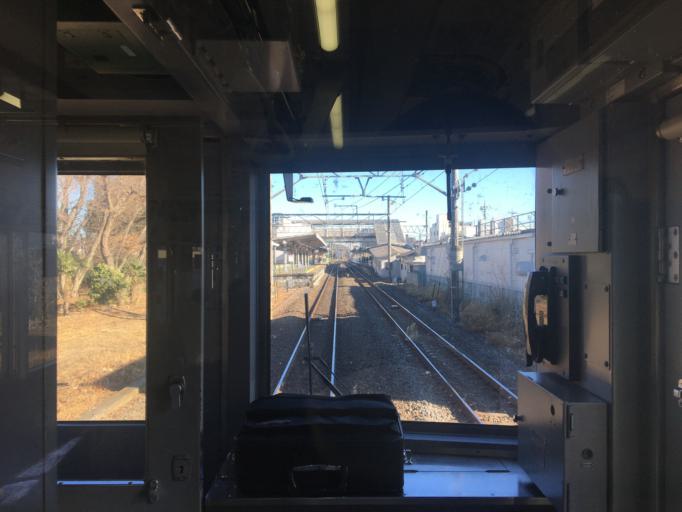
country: JP
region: Saitama
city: Iwatsuki
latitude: 35.9355
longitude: 139.6649
